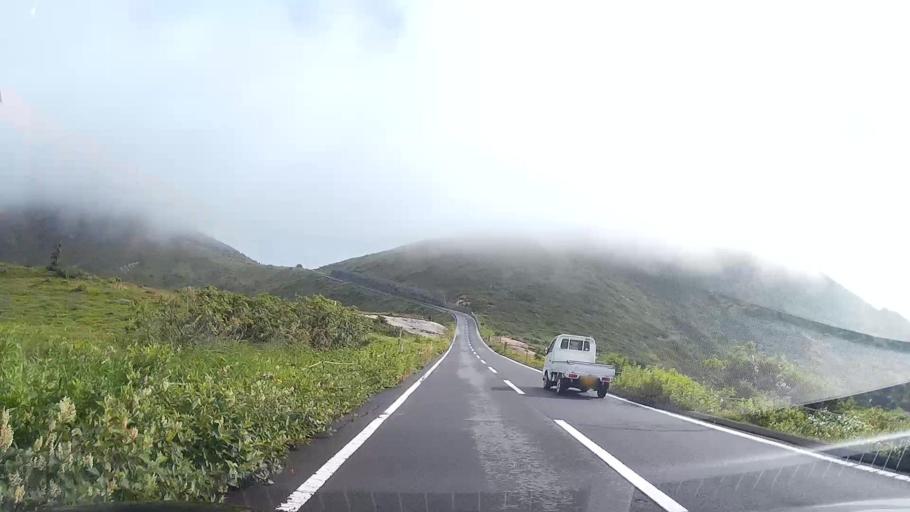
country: JP
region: Nagano
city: Nakano
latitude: 36.6526
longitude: 138.5266
